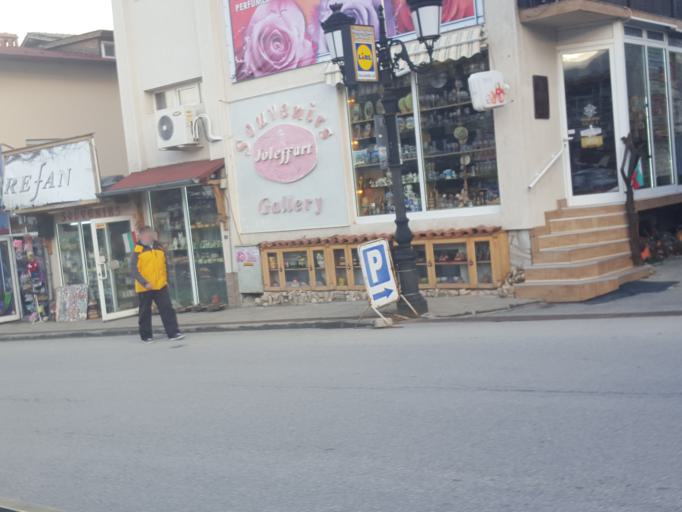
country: BG
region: Blagoevgrad
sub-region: Obshtina Bansko
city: Bansko
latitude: 41.8298
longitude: 23.4807
